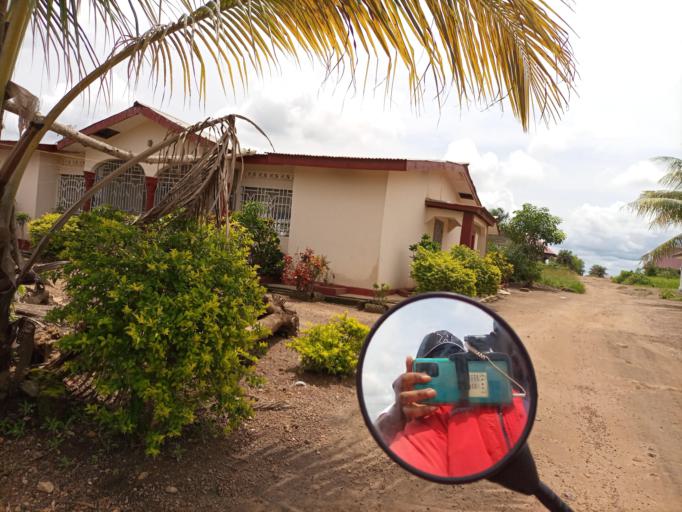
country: SL
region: Southern Province
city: Baoma
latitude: 7.9763
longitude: -11.7203
